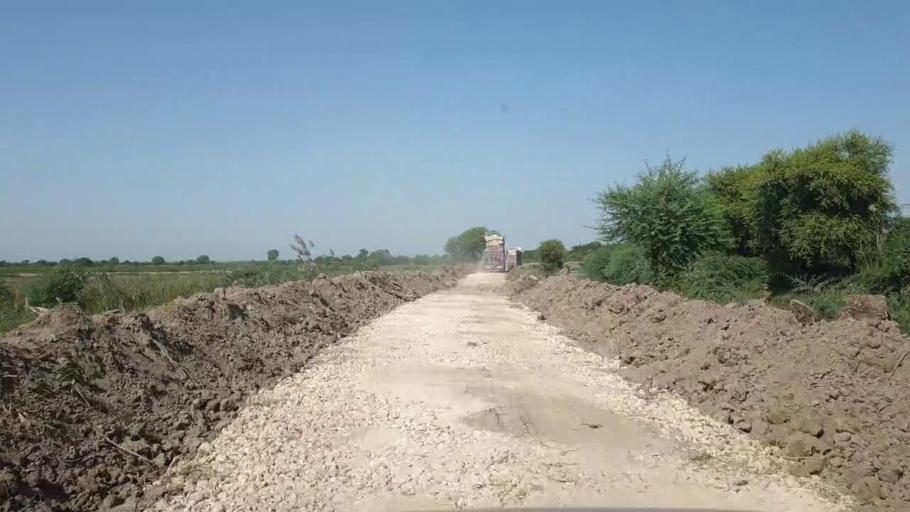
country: PK
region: Sindh
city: Kadhan
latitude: 24.5288
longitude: 69.0005
